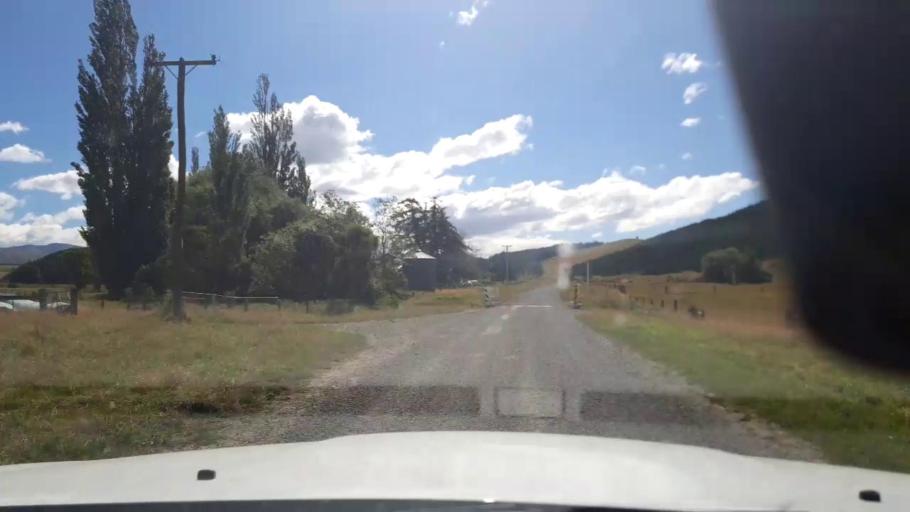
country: NZ
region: Canterbury
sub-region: Timaru District
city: Pleasant Point
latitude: -44.3135
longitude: 170.9222
